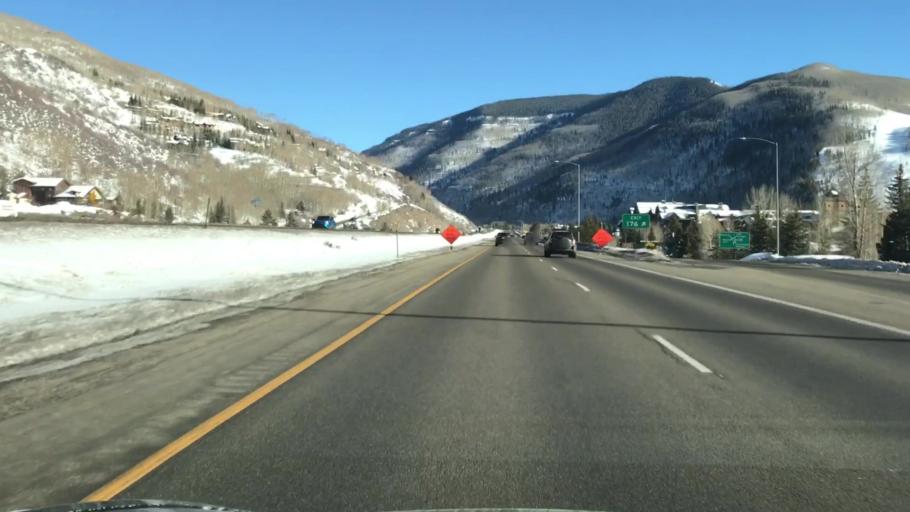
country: US
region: Colorado
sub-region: Eagle County
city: Vail
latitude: 39.6449
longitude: -106.3814
